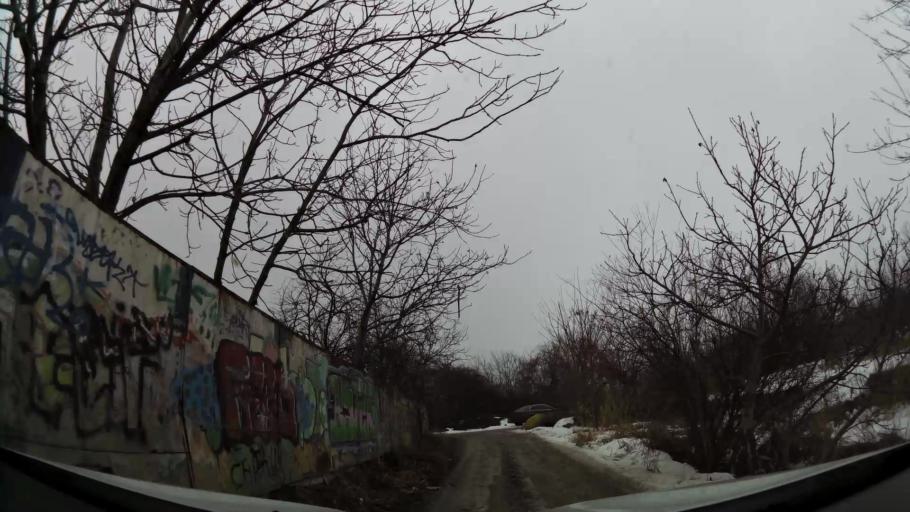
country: RO
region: Ilfov
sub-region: Comuna Popesti-Leordeni
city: Popesti-Leordeni
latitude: 44.4012
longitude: 26.1710
